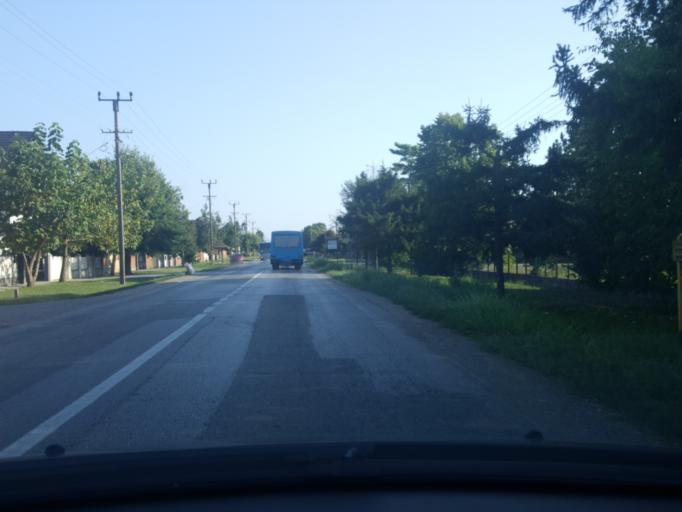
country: RS
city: Hrtkovci
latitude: 44.8849
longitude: 19.7635
